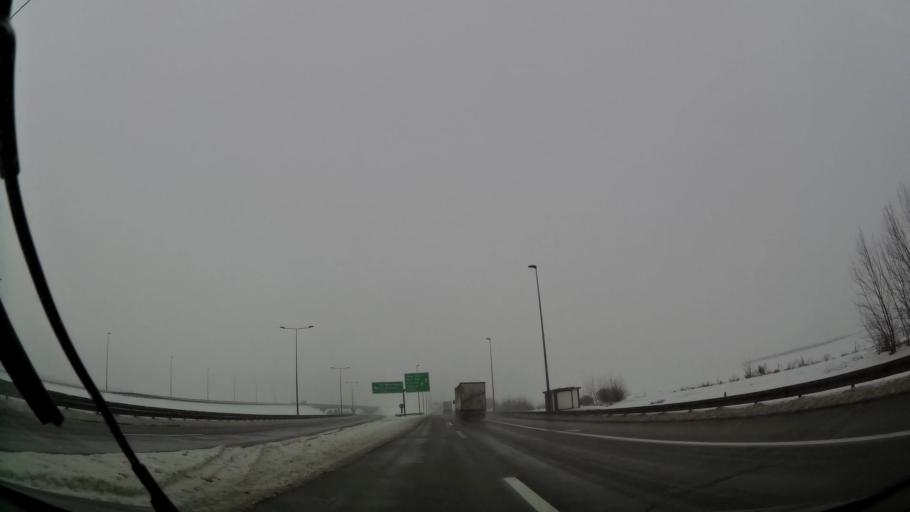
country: RS
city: Dobanovci
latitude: 44.8261
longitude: 20.2519
